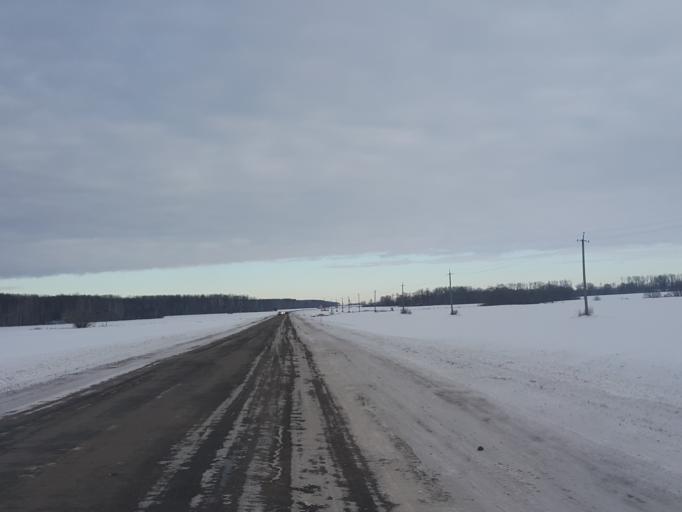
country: RU
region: Tambov
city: Novaya Lyada
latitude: 52.7418
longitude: 41.7043
